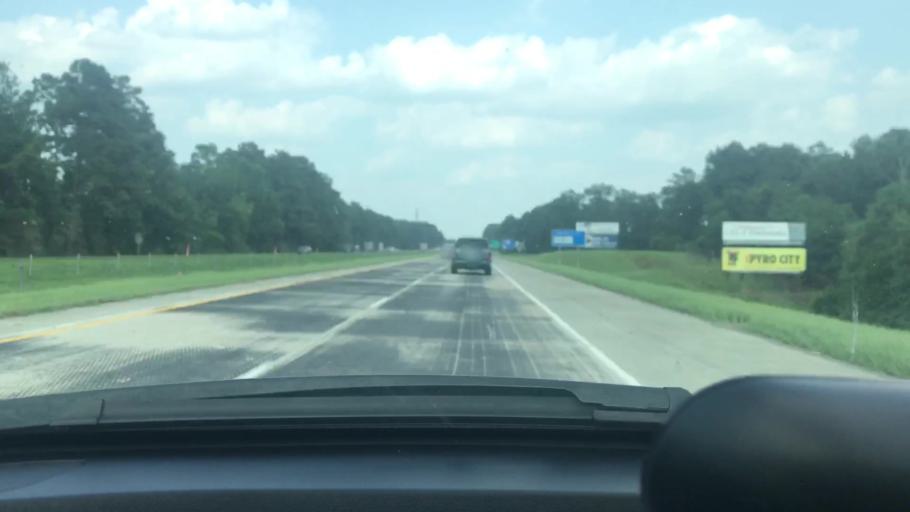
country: US
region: Louisiana
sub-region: Livingston Parish
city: Albany
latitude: 30.4790
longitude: -90.5531
